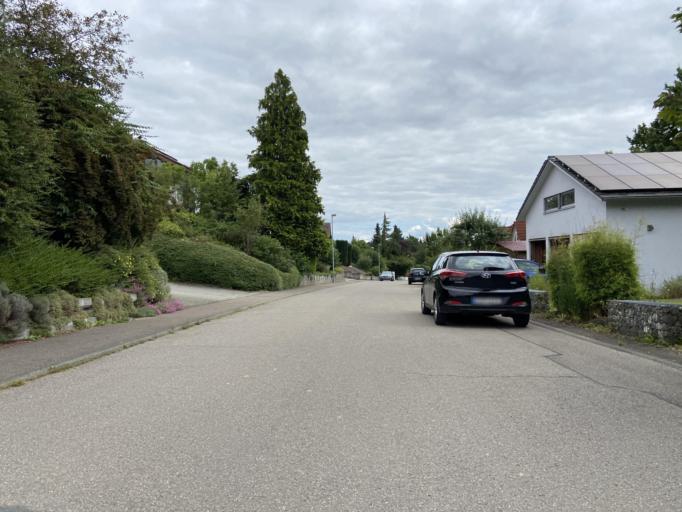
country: DE
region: Baden-Wuerttemberg
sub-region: Tuebingen Region
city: Sigmaringendorf
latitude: 48.0737
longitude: 9.2559
